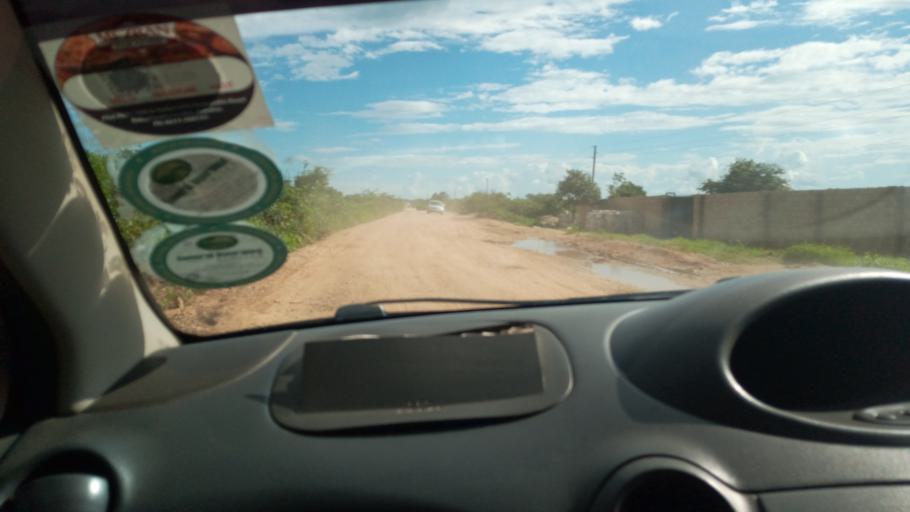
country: ZM
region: Lusaka
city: Lusaka
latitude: -15.5169
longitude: 28.3422
